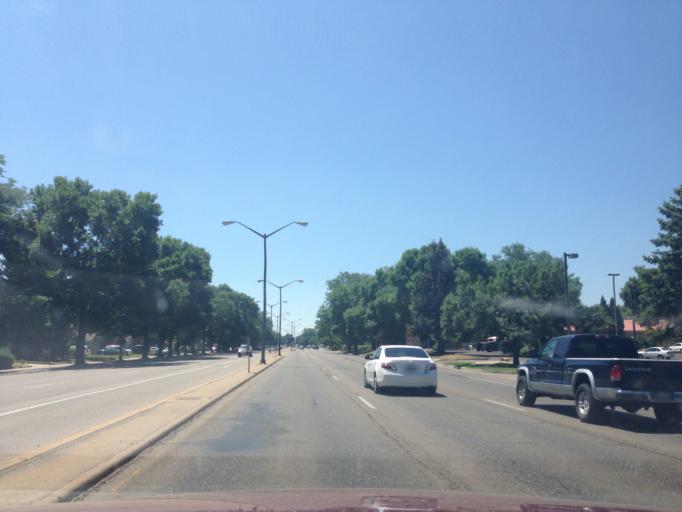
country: US
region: Colorado
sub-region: Larimer County
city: Fort Collins
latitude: 40.5562
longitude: -105.0771
